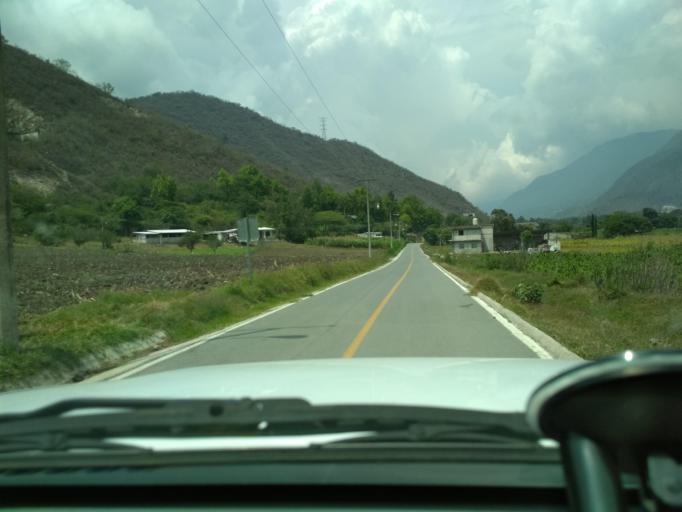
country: MX
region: Veracruz
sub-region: Nogales
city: Taza de Agua Ojo Zarco
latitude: 18.7794
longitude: -97.2195
